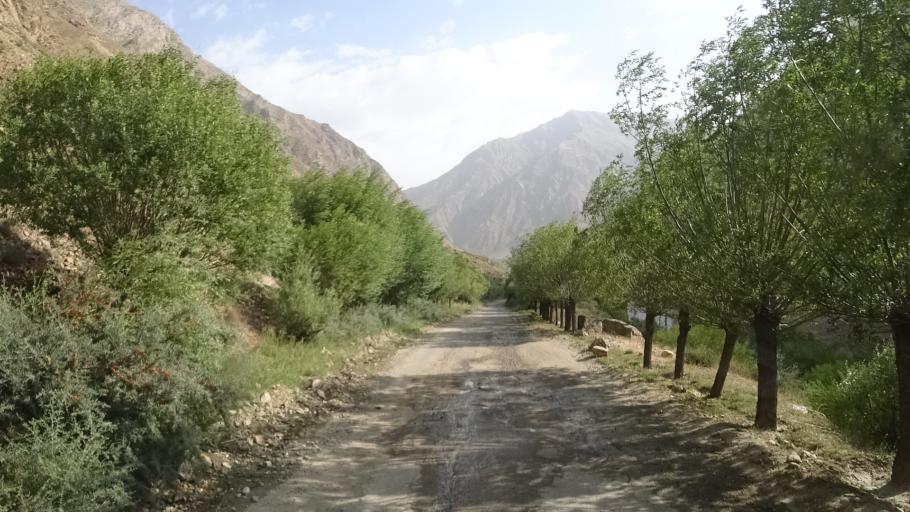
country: TJ
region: Gorno-Badakhshan
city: Khorugh
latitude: 37.3524
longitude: 71.4937
